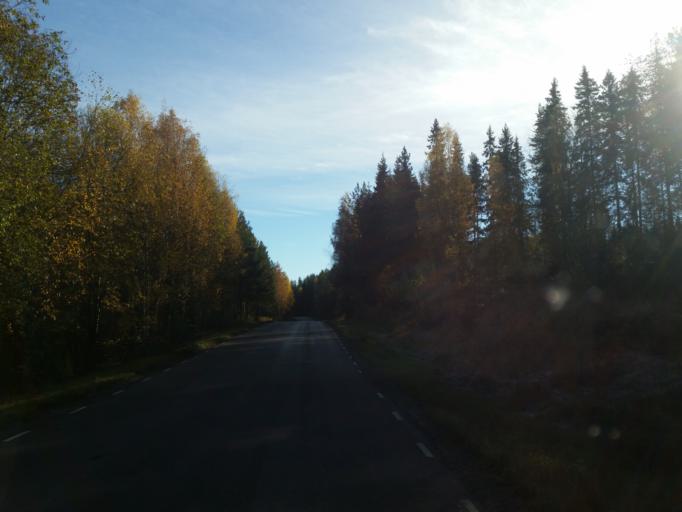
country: SE
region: Dalarna
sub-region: Borlange Kommun
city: Ornas
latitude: 60.5205
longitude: 15.5132
